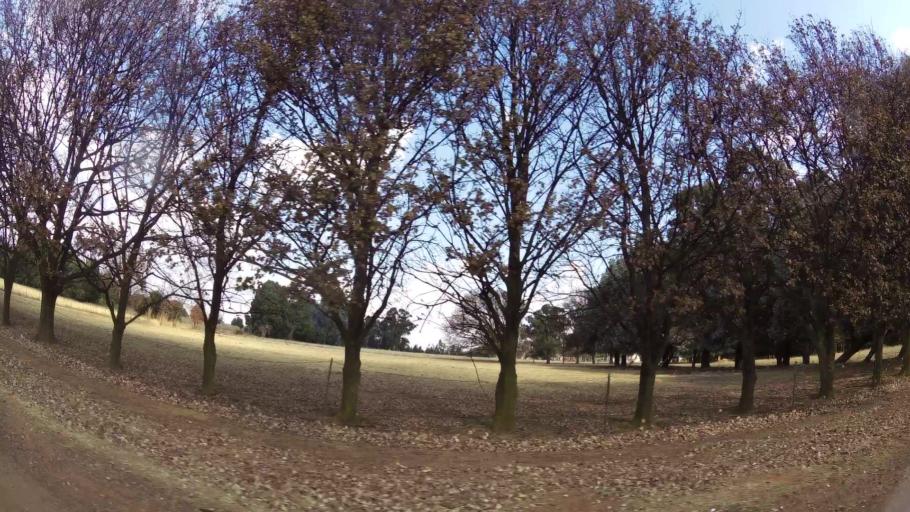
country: ZA
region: Mpumalanga
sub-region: Nkangala District Municipality
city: Delmas
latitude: -26.1493
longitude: 28.5558
